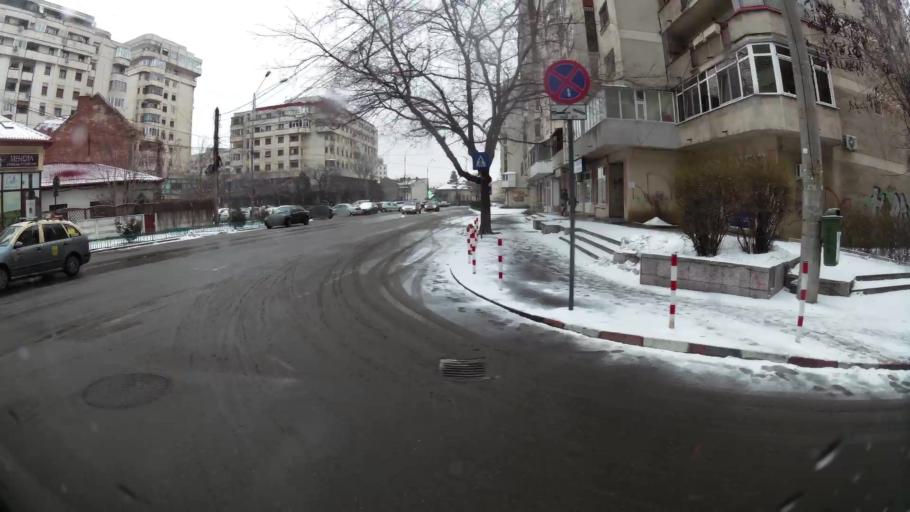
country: RO
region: Prahova
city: Ploiesti
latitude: 44.9409
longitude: 26.0185
